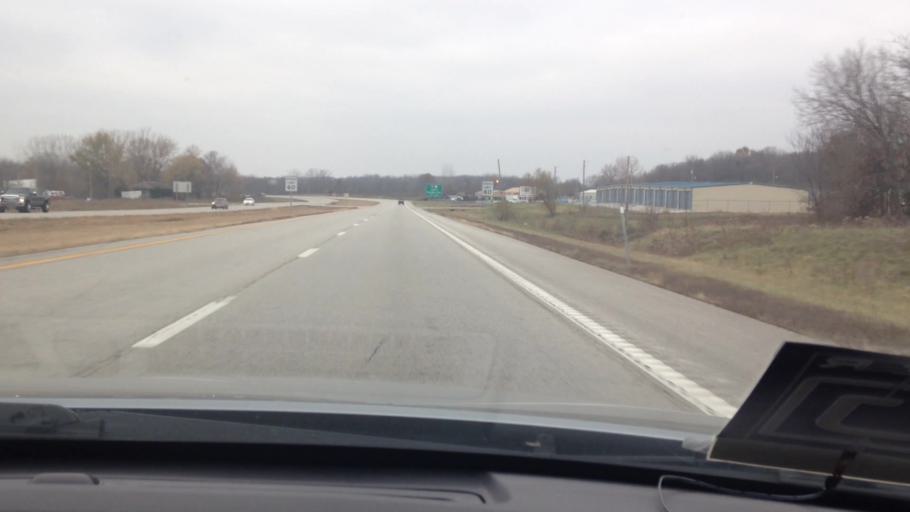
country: US
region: Missouri
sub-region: Cass County
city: Harrisonville
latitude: 38.6141
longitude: -94.3274
